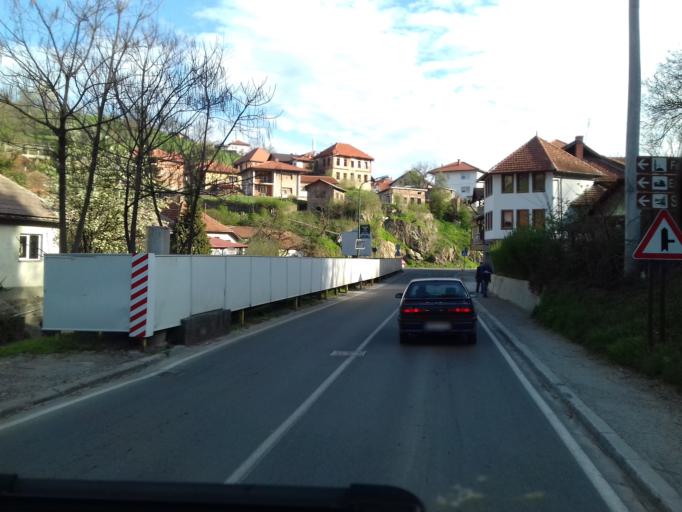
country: BA
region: Federation of Bosnia and Herzegovina
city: Tesanj
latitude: 44.6141
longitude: 17.9908
